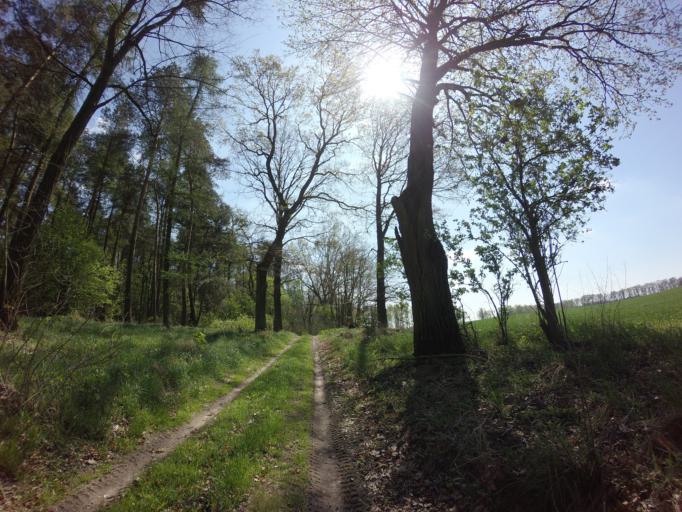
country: PL
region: West Pomeranian Voivodeship
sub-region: Powiat stargardzki
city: Suchan
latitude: 53.2038
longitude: 15.3059
